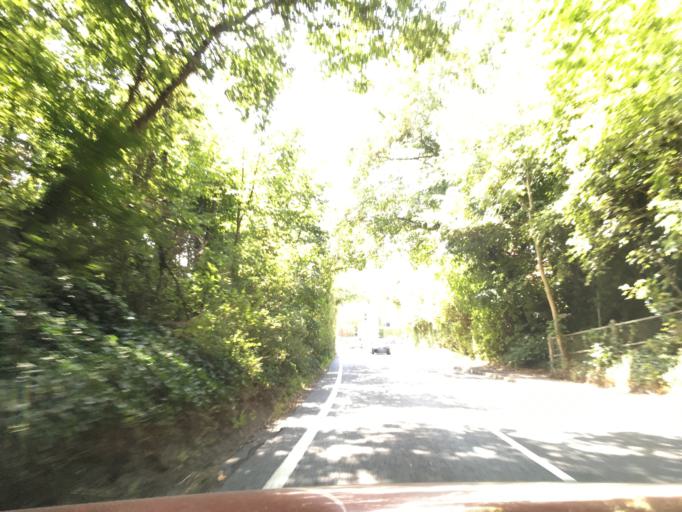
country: GB
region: England
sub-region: Hampshire
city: Colden Common
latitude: 51.0197
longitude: -1.3144
